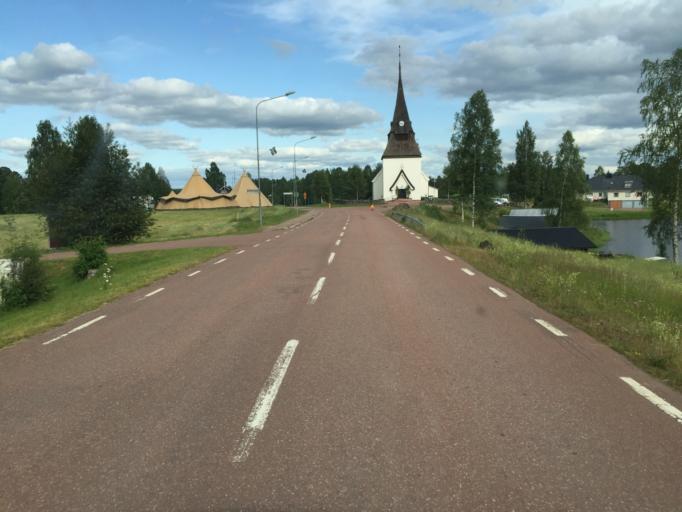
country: SE
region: Dalarna
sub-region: Alvdalens Kommun
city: AElvdalen
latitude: 60.9512
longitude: 13.9051
